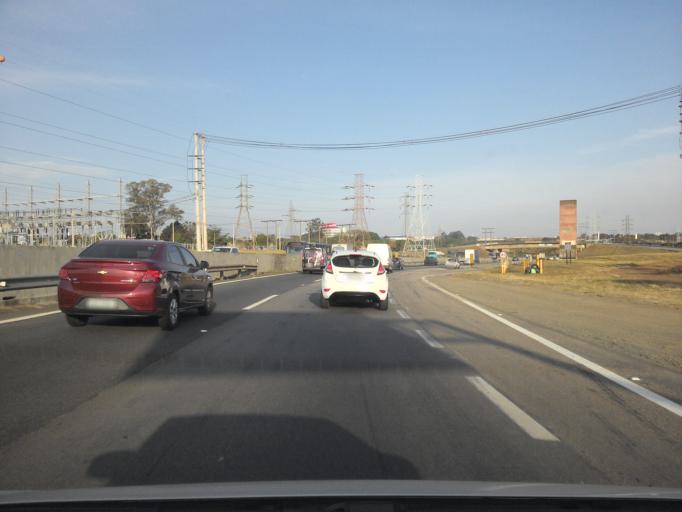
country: BR
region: Sao Paulo
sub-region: Campinas
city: Campinas
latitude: -22.8934
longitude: -47.1257
